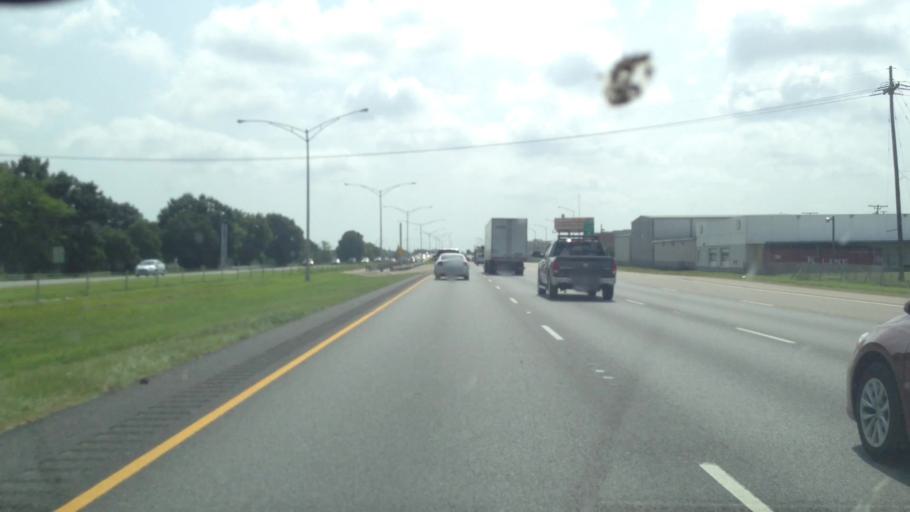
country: US
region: Louisiana
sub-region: Jefferson Parish
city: Kenner
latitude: 30.0068
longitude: -90.2754
